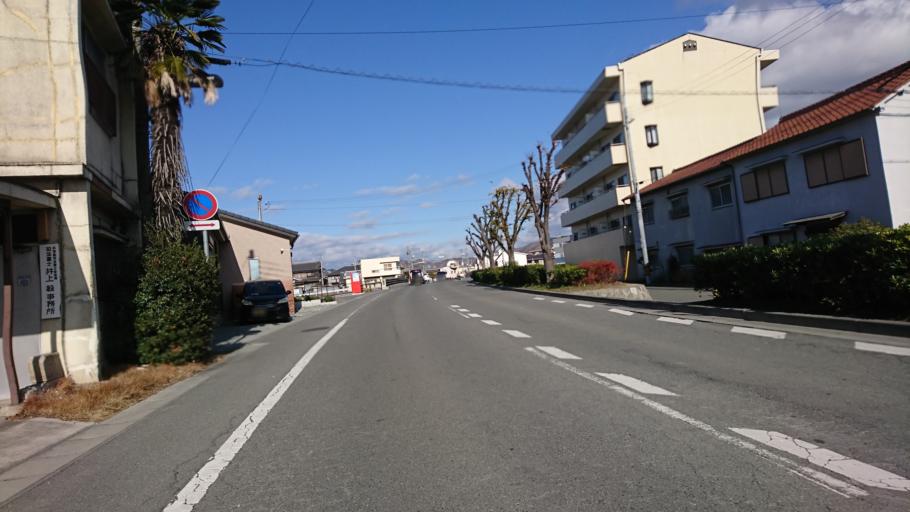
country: JP
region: Hyogo
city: Kakogawacho-honmachi
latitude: 34.7653
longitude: 134.7882
